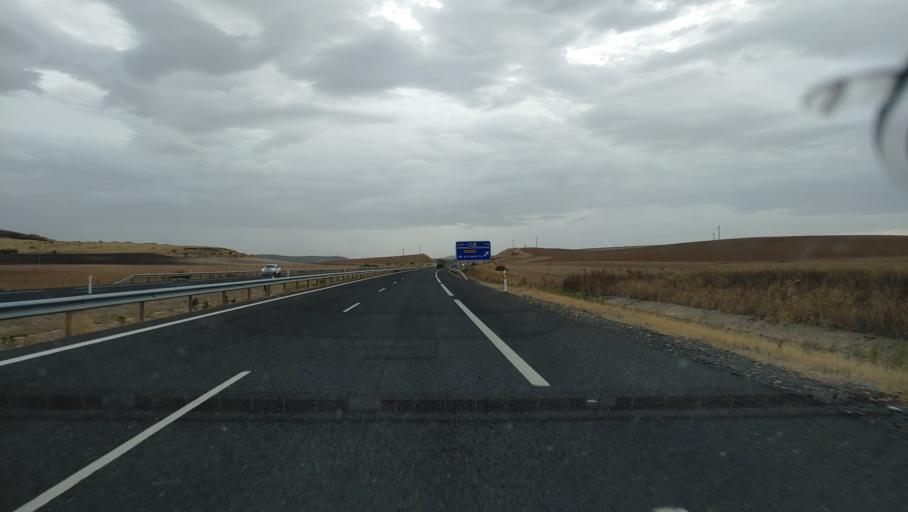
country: ES
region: Castille-La Mancha
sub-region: Provincia de Ciudad Real
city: Canada de Calatrava
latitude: 38.8915
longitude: -3.9991
